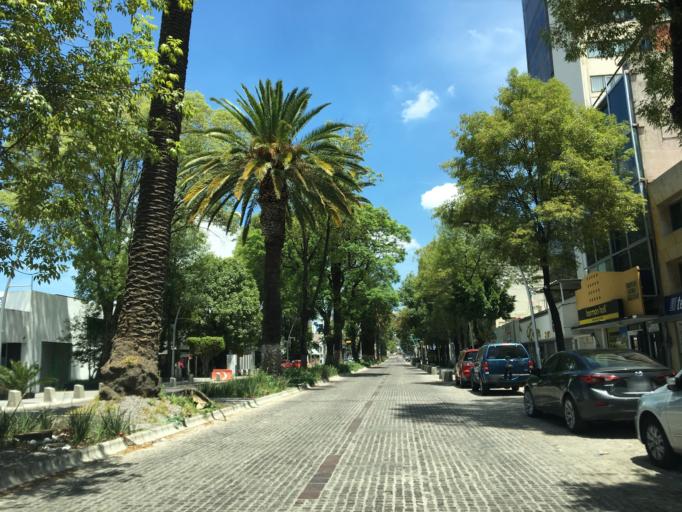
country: MX
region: Puebla
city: Puebla
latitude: 19.0500
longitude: -98.2150
